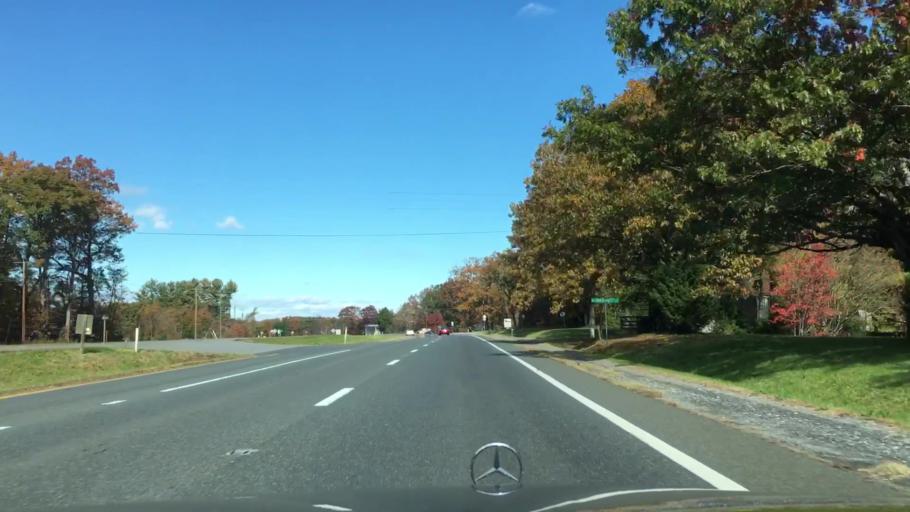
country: US
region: Virginia
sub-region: Campbell County
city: Rustburg
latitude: 37.2339
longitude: -79.1856
